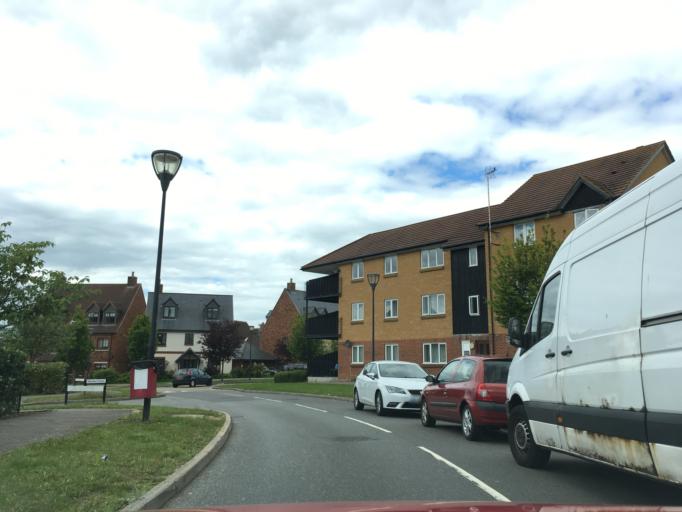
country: GB
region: England
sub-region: Milton Keynes
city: Simpson
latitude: 52.0352
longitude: -0.7104
